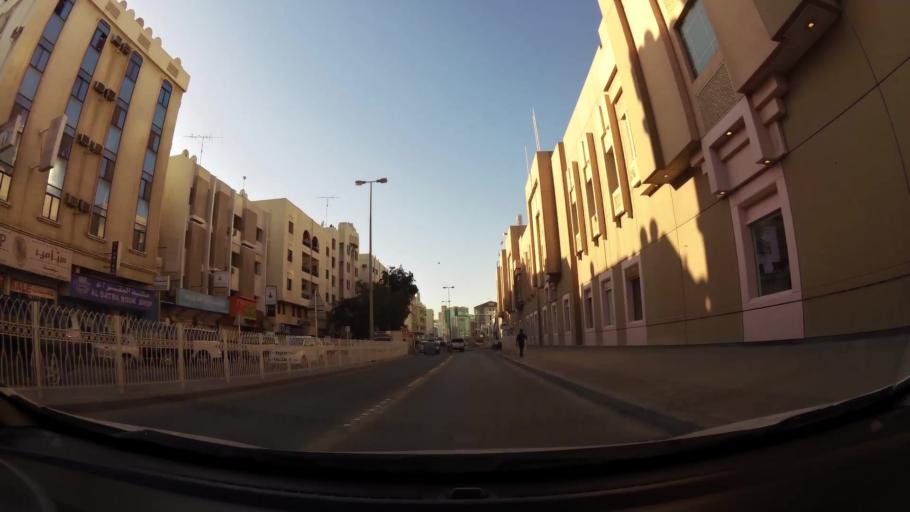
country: BH
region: Manama
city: Manama
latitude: 26.2356
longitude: 50.5930
